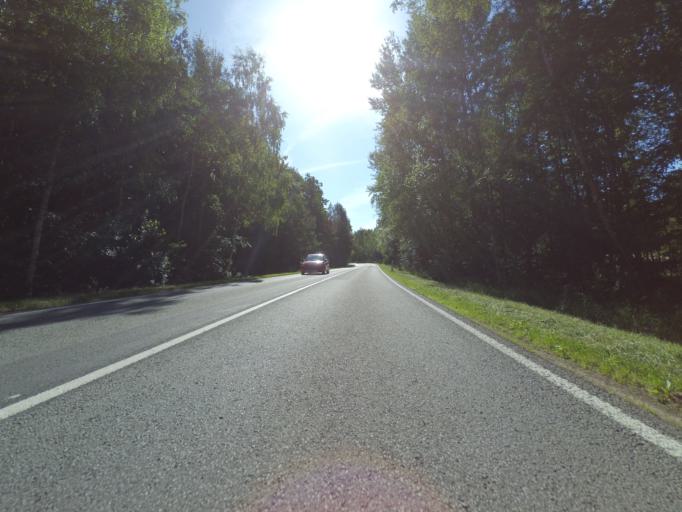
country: DE
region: Brandenburg
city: Putlitz
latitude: 53.2792
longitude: 12.0772
